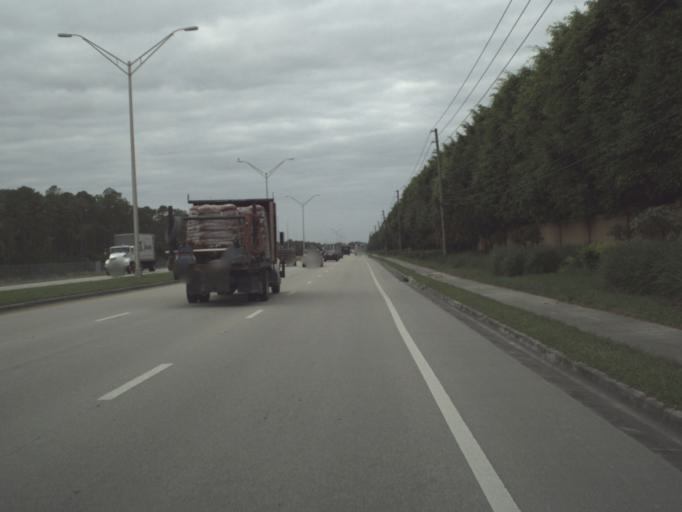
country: US
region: Florida
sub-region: Collier County
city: Lely Resort
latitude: 26.0734
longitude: -81.6915
